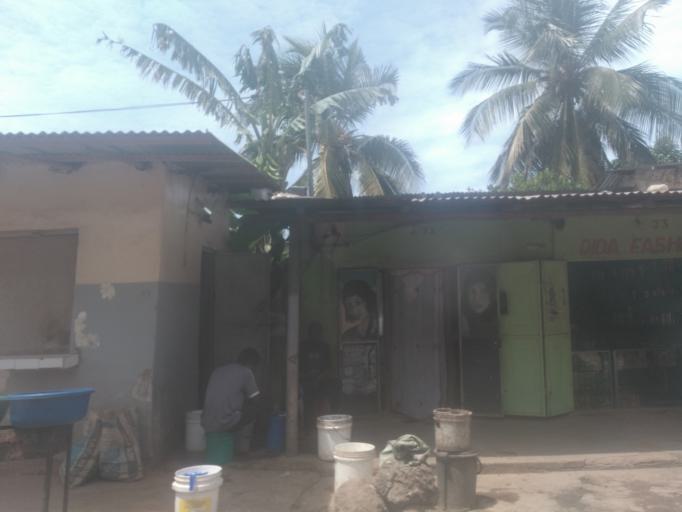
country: TZ
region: Zanzibar Urban/West
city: Zanzibar
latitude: -6.2276
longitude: 39.2144
